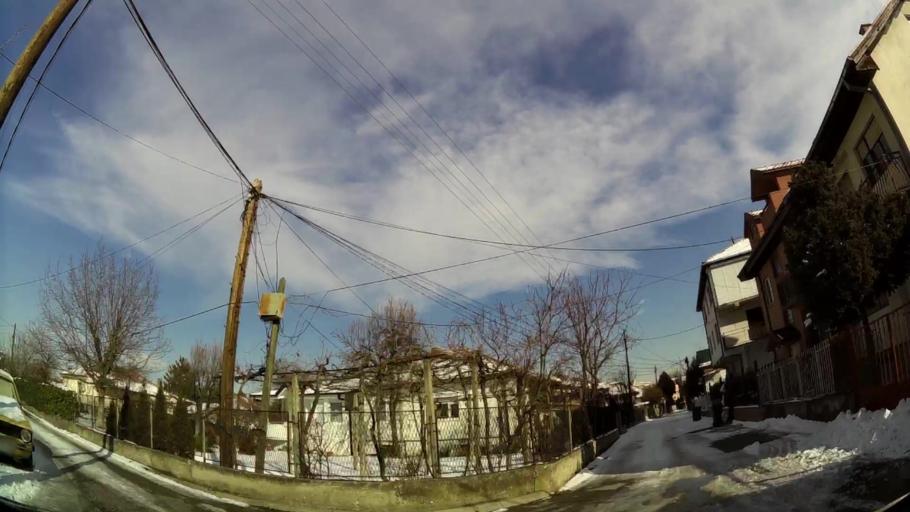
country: MK
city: Krushopek
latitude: 41.9996
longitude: 21.3728
